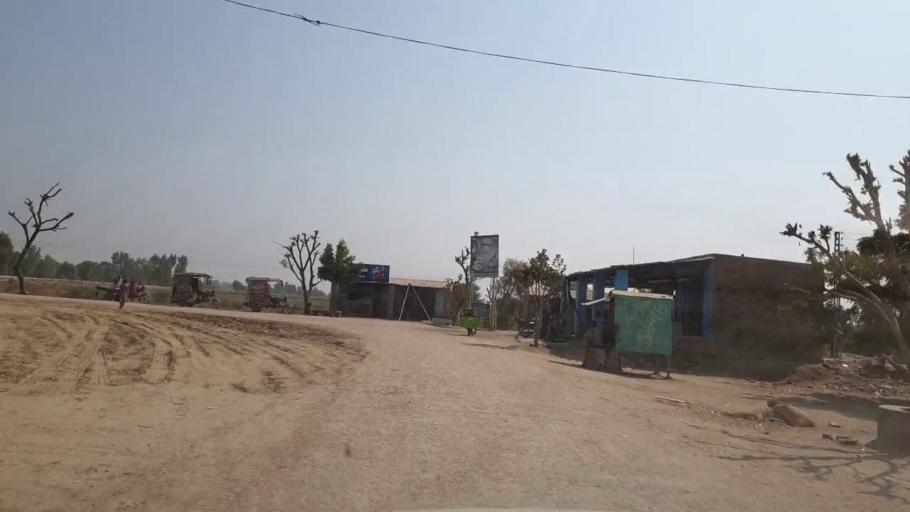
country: PK
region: Sindh
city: Mirpur Khas
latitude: 25.6490
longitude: 69.1487
